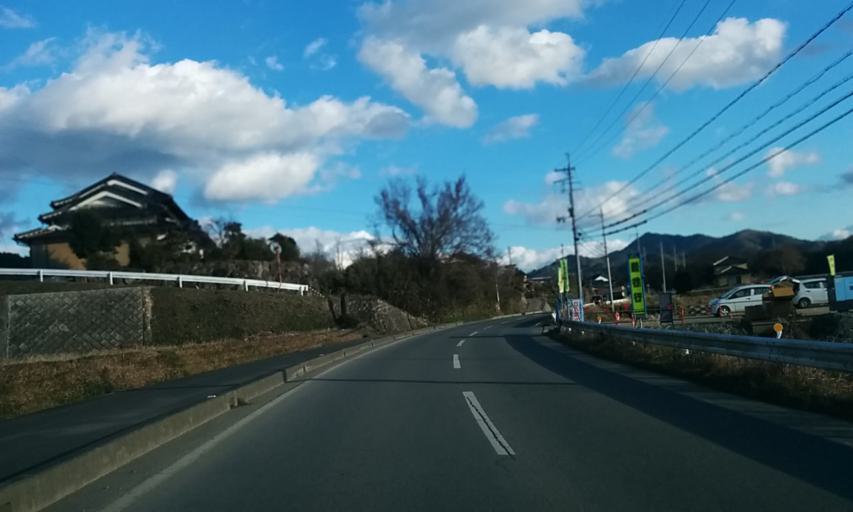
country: JP
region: Kyoto
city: Fukuchiyama
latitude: 35.3122
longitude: 135.1645
